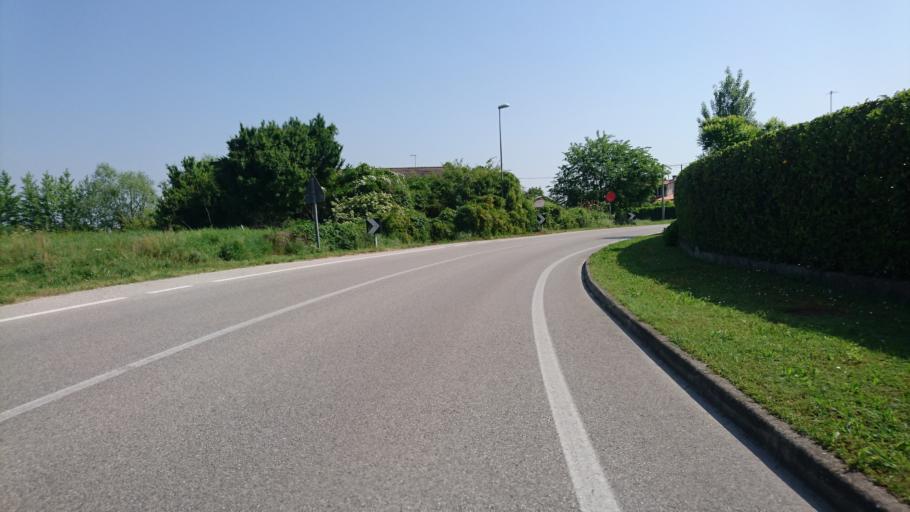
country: IT
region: Veneto
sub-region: Provincia di Venezia
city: Campagna Lupia
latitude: 45.3607
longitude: 12.1099
